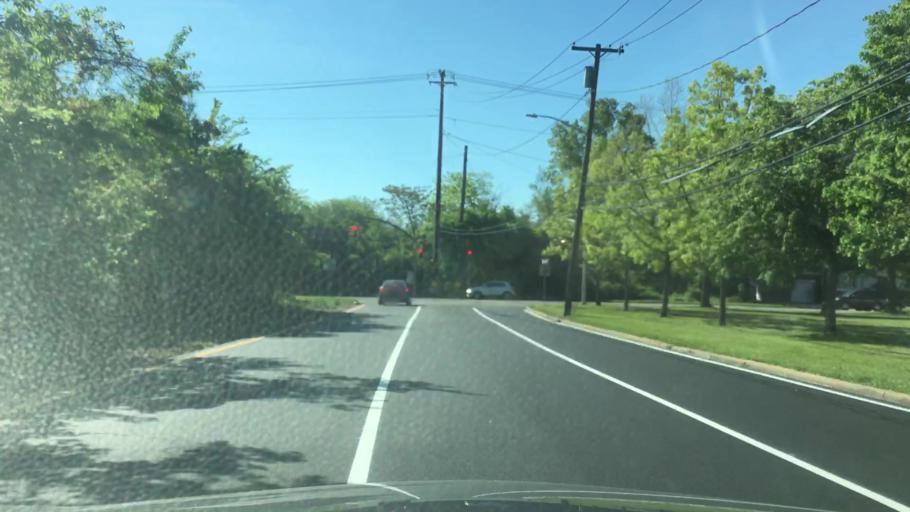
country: US
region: New York
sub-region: Nassau County
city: Plainview
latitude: 40.7971
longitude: -73.4888
